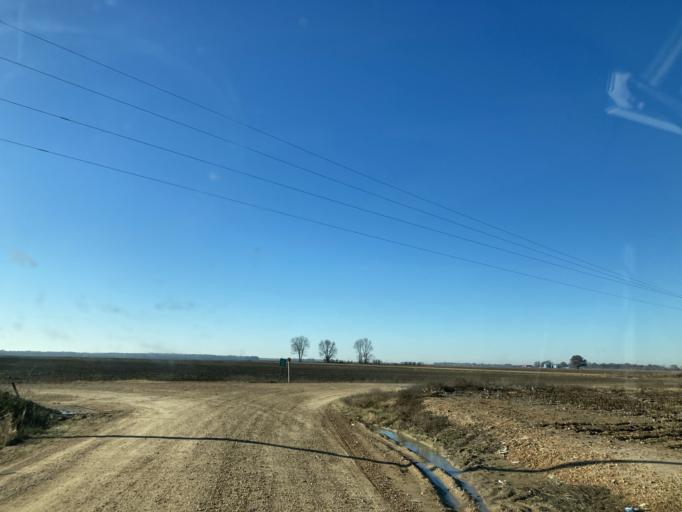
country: US
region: Mississippi
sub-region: Yazoo County
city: Yazoo City
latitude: 32.9229
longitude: -90.5921
